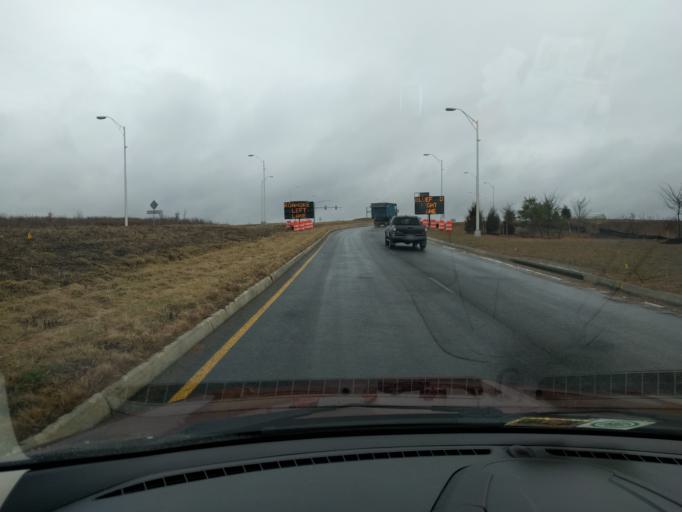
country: US
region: Virginia
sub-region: Montgomery County
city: Blacksburg
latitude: 37.2117
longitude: -80.4257
